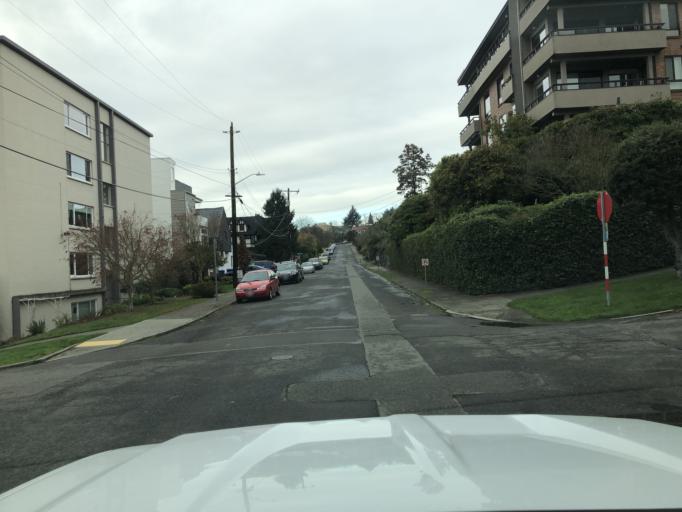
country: US
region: Washington
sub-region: King County
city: Seattle
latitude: 47.6277
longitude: -122.3592
